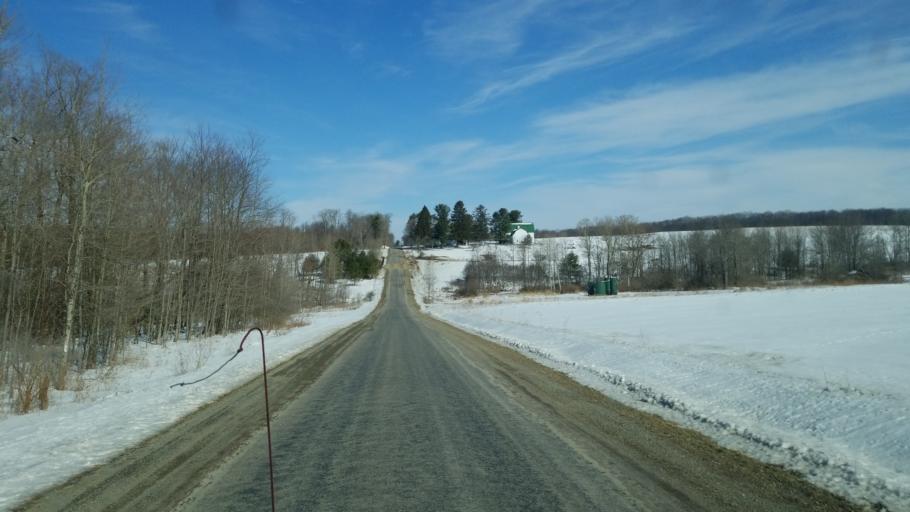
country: US
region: New York
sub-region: Allegany County
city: Andover
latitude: 42.0771
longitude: -77.7718
